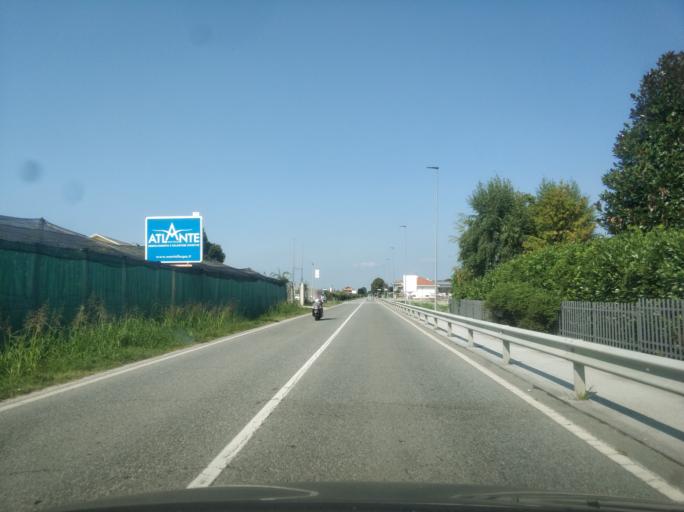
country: IT
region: Piedmont
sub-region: Provincia di Cuneo
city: Centallo
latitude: 44.5065
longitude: 7.5879
